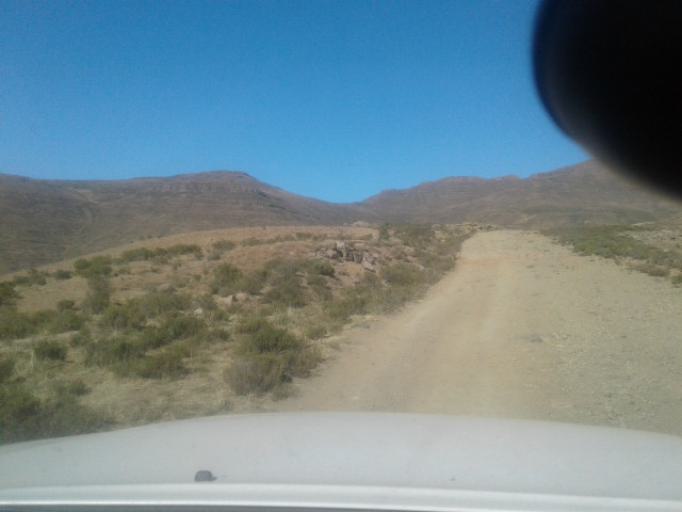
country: LS
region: Maseru
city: Nako
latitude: -29.3939
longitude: 28.0034
